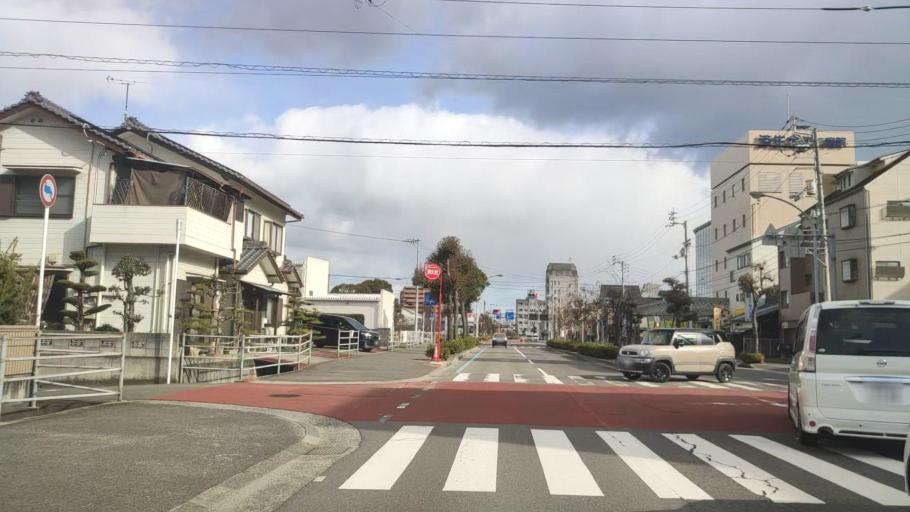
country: JP
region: Ehime
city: Hojo
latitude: 34.0633
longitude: 132.9874
